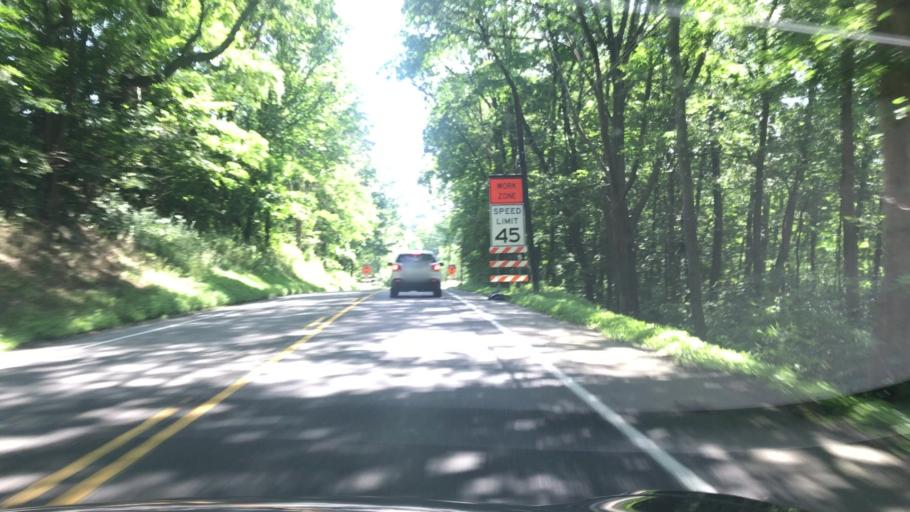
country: US
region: Pennsylvania
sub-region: Lycoming County
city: Garden View
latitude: 41.4215
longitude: -77.0294
